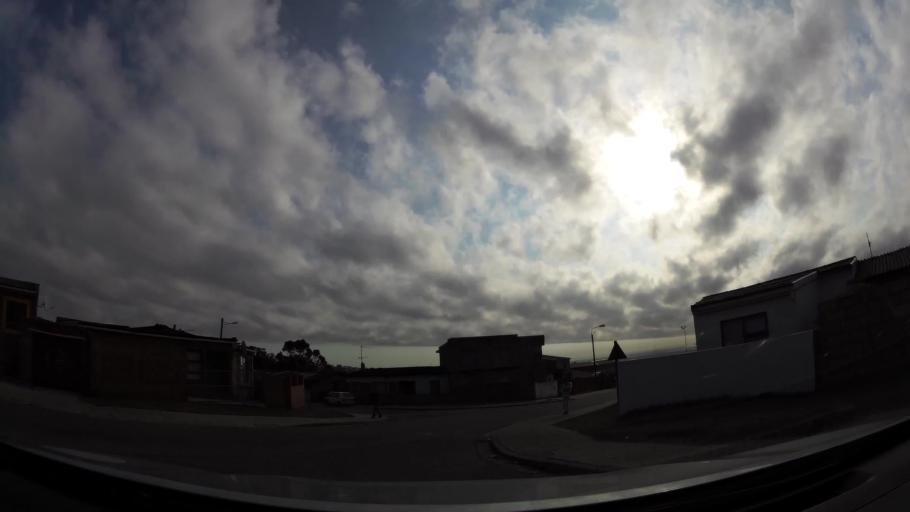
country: ZA
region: Eastern Cape
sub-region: Nelson Mandela Bay Metropolitan Municipality
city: Port Elizabeth
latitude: -33.9168
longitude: 25.5459
